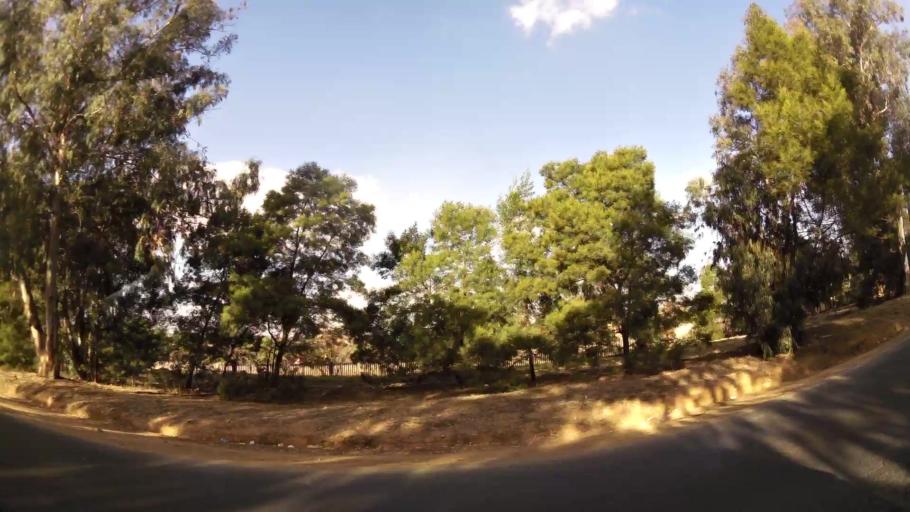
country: ZA
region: Gauteng
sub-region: City of Johannesburg Metropolitan Municipality
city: Midrand
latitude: -25.9678
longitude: 28.1373
